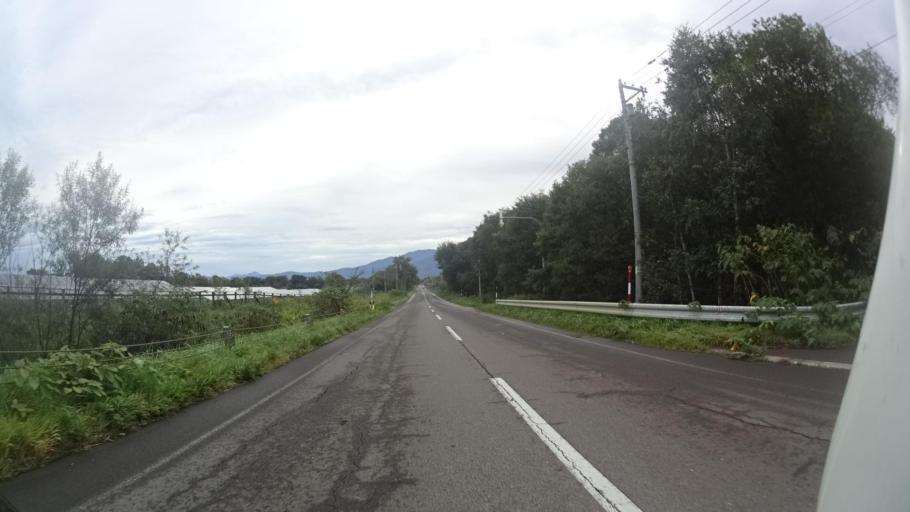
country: JP
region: Hokkaido
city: Abashiri
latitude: 43.8711
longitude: 144.6721
